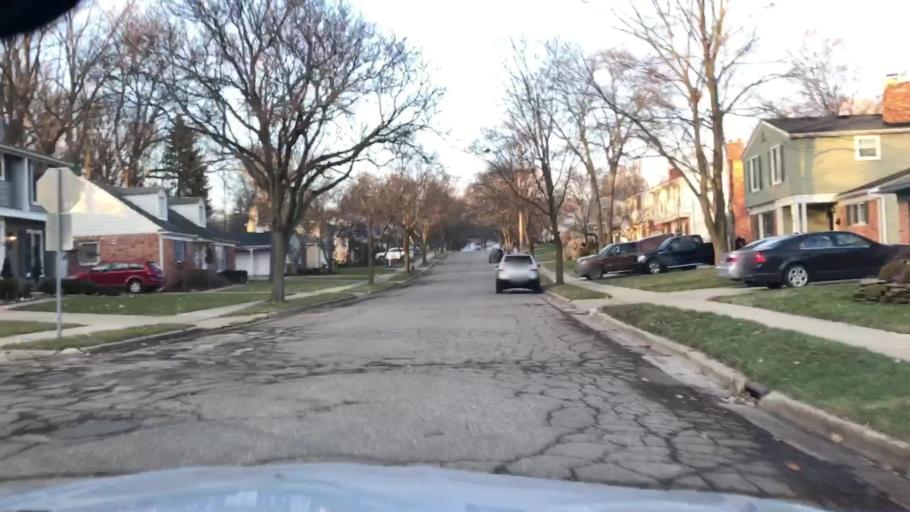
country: US
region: Michigan
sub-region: Wayne County
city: Northville
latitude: 42.4412
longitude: -83.4785
